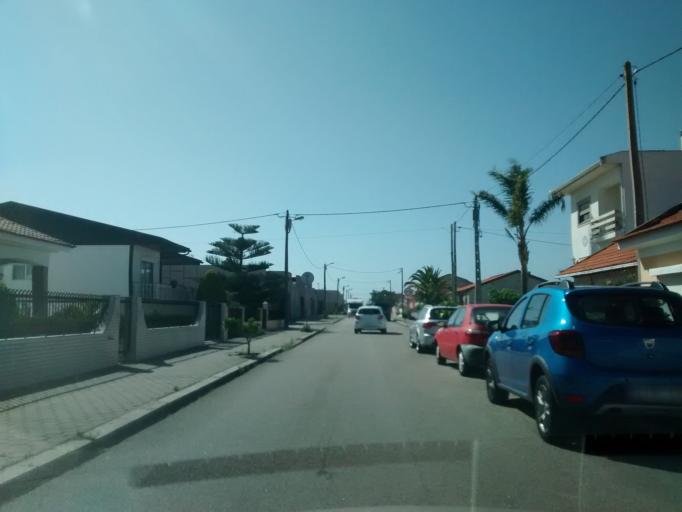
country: PT
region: Aveiro
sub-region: Ilhavo
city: Gafanha da Nazare
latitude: 40.6649
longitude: -8.7325
